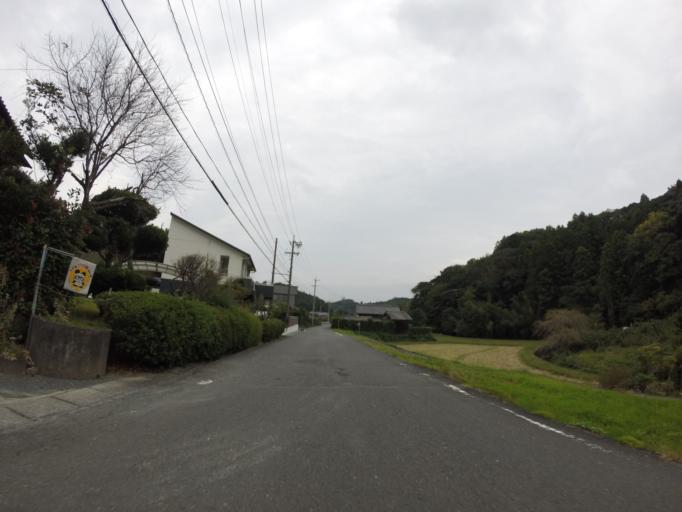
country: JP
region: Shizuoka
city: Kakegawa
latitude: 34.8212
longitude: 138.0159
